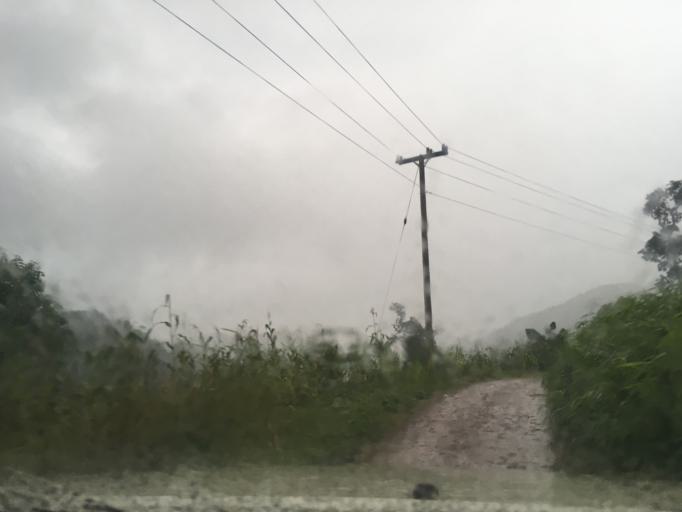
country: LA
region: Oudomxai
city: Muang La
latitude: 21.2381
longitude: 101.9559
